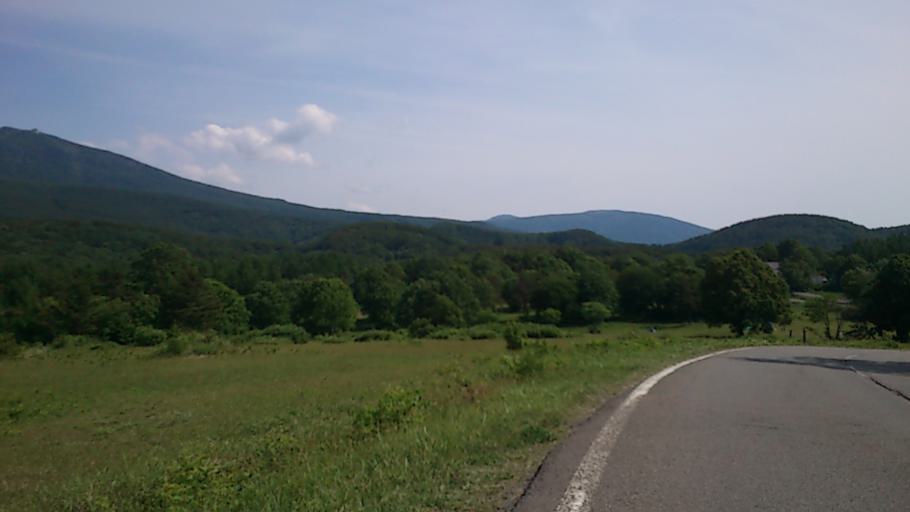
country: JP
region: Aomori
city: Aomori Shi
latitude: 40.7129
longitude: 140.8245
